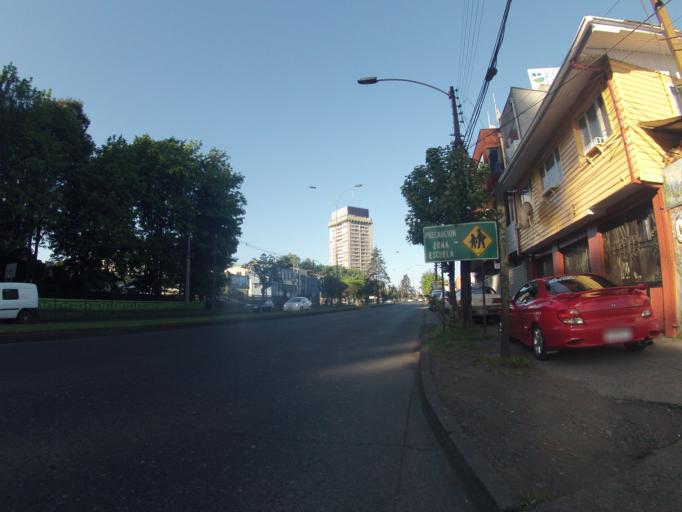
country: CL
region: Araucania
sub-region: Provincia de Cautin
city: Temuco
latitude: -38.7405
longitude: -72.6020
